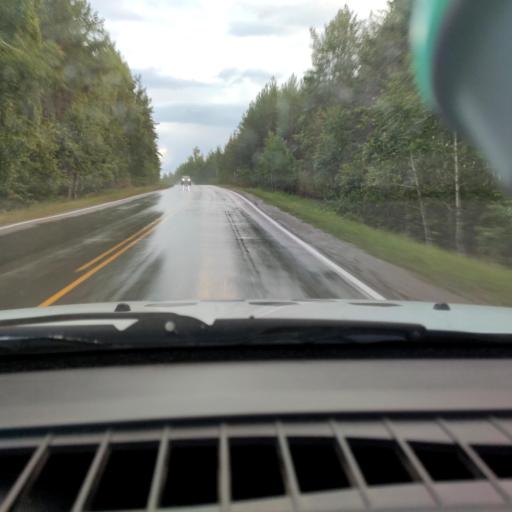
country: RU
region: Chelyabinsk
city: Kyshtym
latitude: 55.7385
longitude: 60.5434
